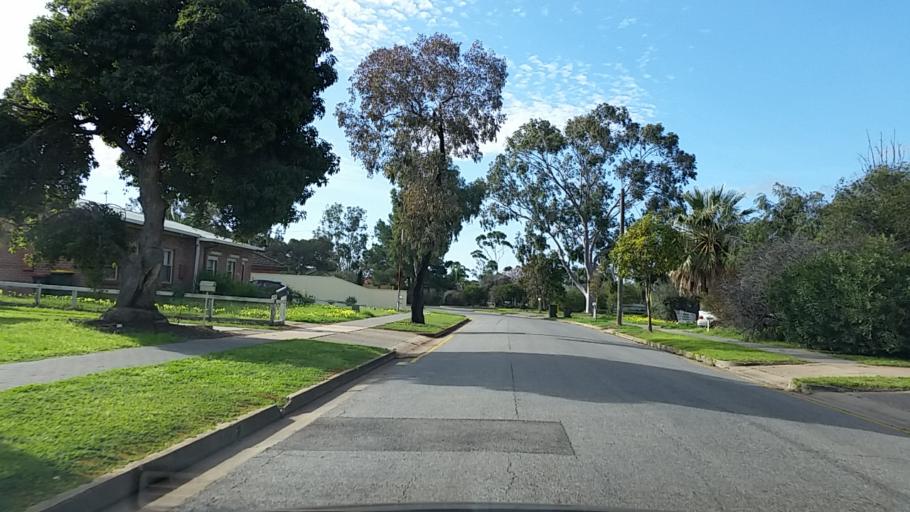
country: AU
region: South Australia
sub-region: Salisbury
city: Elizabeth
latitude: -34.7301
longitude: 138.6665
